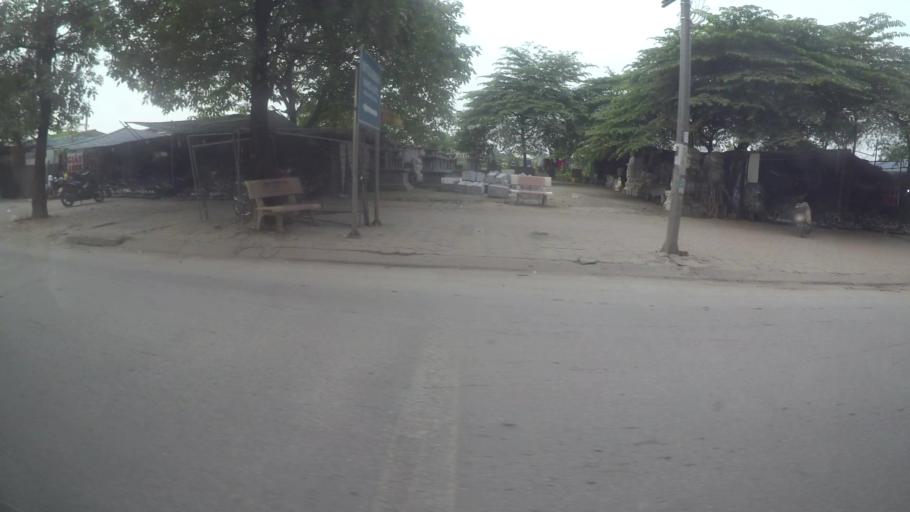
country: VN
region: Ha Noi
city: Cau Dien
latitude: 21.0483
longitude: 105.7445
